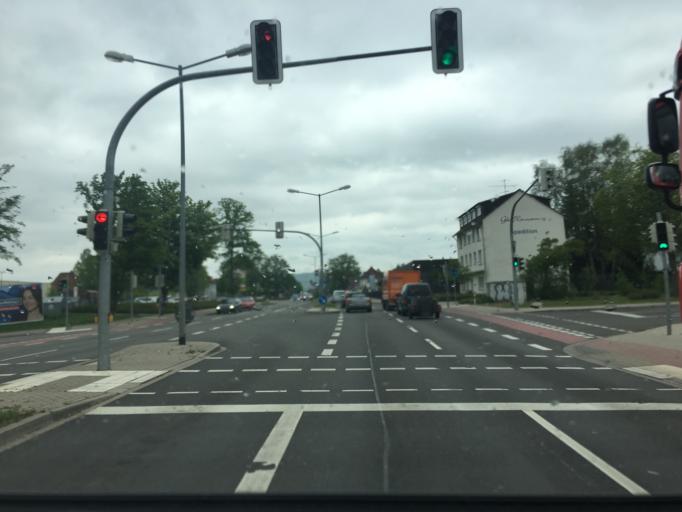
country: DE
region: North Rhine-Westphalia
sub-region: Regierungsbezirk Detmold
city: Minden
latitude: 52.2931
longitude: 8.9020
